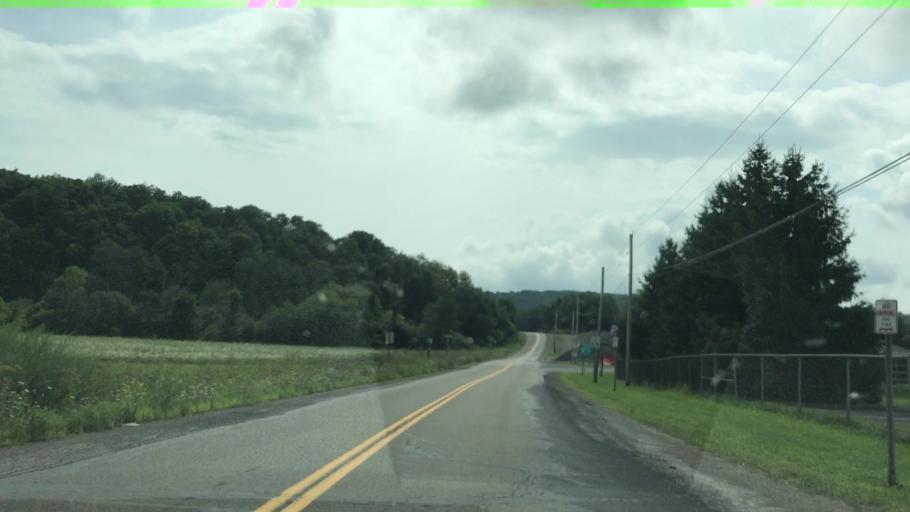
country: US
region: New York
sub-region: Ontario County
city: Naples
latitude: 42.5098
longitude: -77.2768
